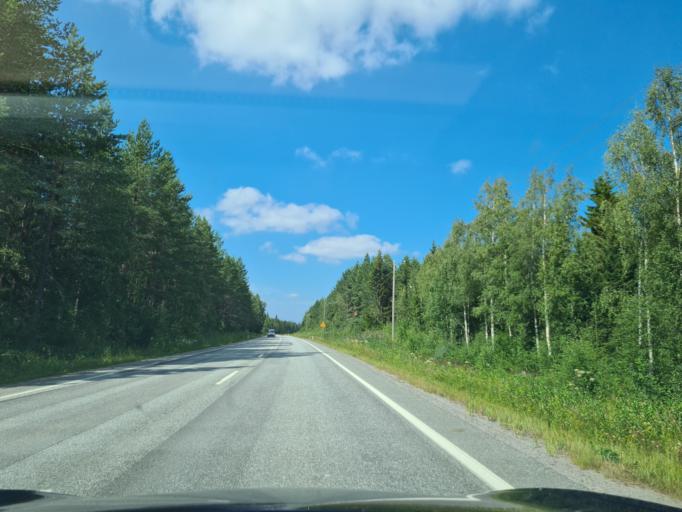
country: FI
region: Ostrobothnia
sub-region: Vaasa
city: Vaasa
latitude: 63.1798
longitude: 21.5738
